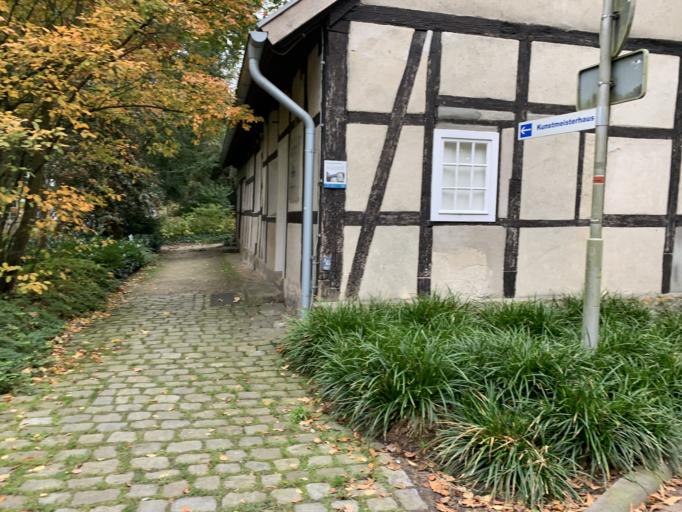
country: DE
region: North Rhine-Westphalia
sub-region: Regierungsbezirk Munster
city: Rheine
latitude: 52.2986
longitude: 7.4194
